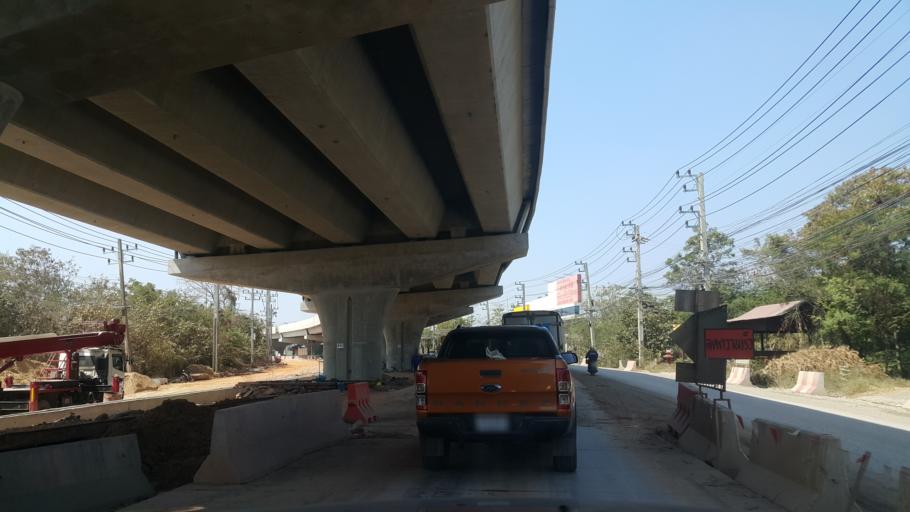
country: TH
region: Nakhon Ratchasima
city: Bua Yai
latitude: 15.5921
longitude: 102.4315
